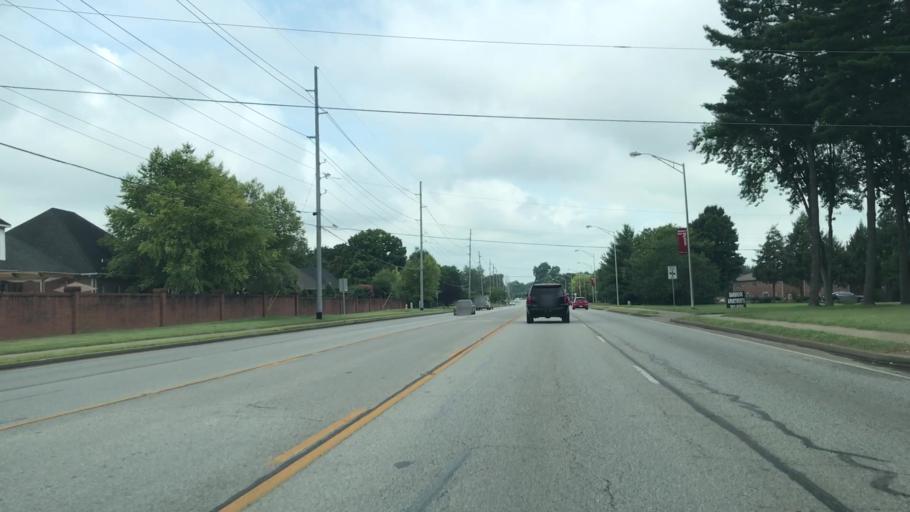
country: US
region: Kentucky
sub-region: Warren County
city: Bowling Green
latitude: 36.9888
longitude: -86.4080
